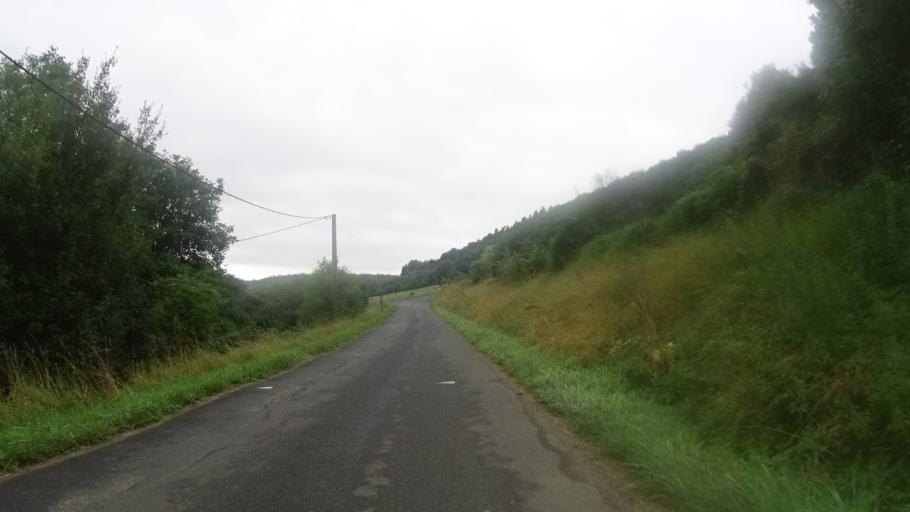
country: FR
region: Lorraine
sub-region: Departement de Meurthe-et-Moselle
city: Chaligny
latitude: 48.6337
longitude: 6.0405
